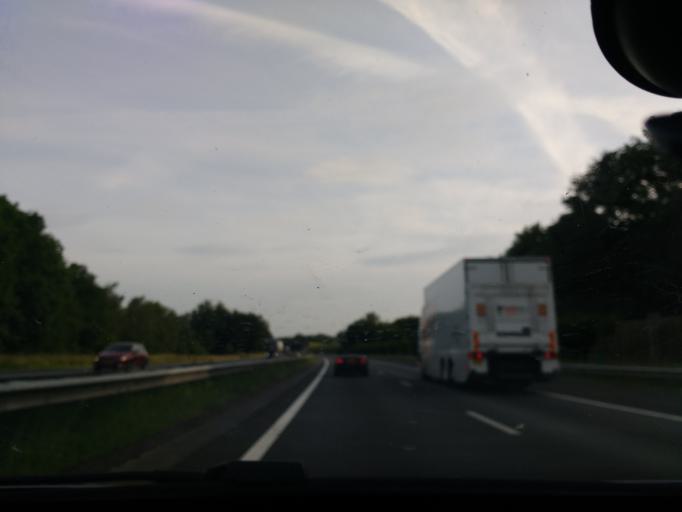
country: NL
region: Gelderland
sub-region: Gemeente Wijchen
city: Bergharen
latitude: 51.8338
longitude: 5.6857
